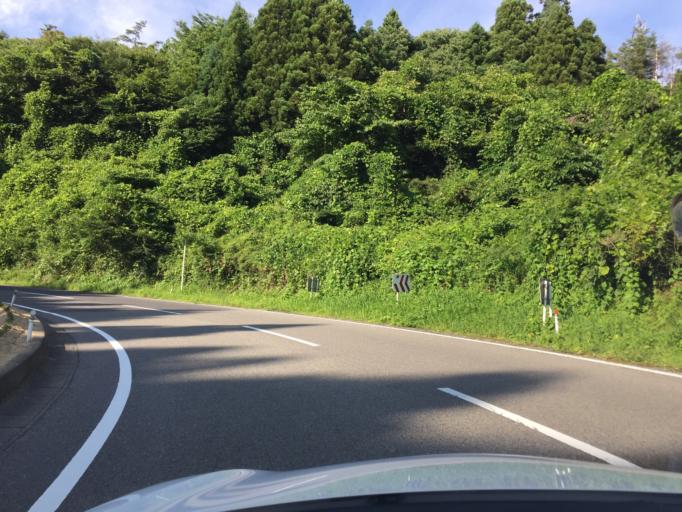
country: JP
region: Fukushima
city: Sukagawa
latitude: 37.3142
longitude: 140.4868
